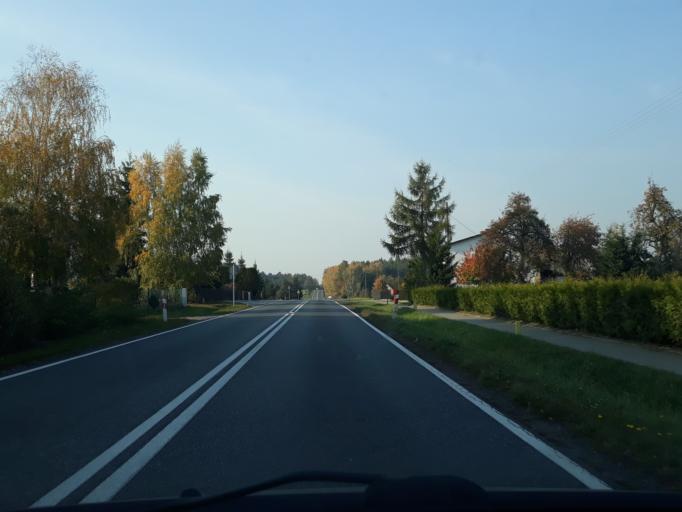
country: PL
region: Kujawsko-Pomorskie
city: Kamien Krajenski
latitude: 53.5408
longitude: 17.5182
